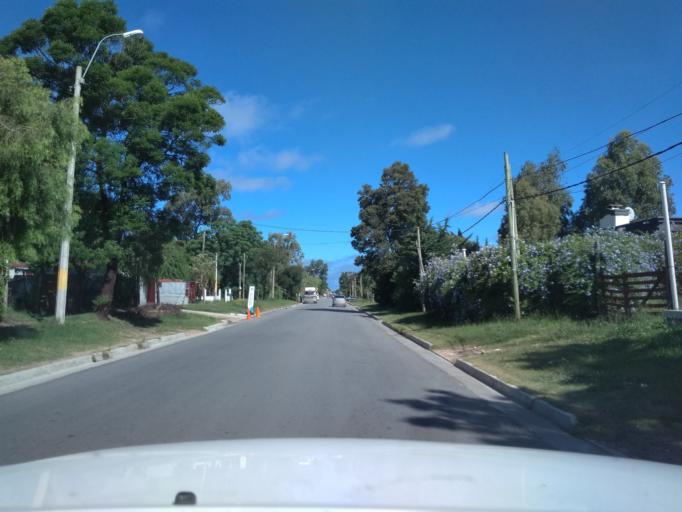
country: UY
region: Canelones
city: Colonia Nicolich
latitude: -34.8242
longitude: -55.9719
